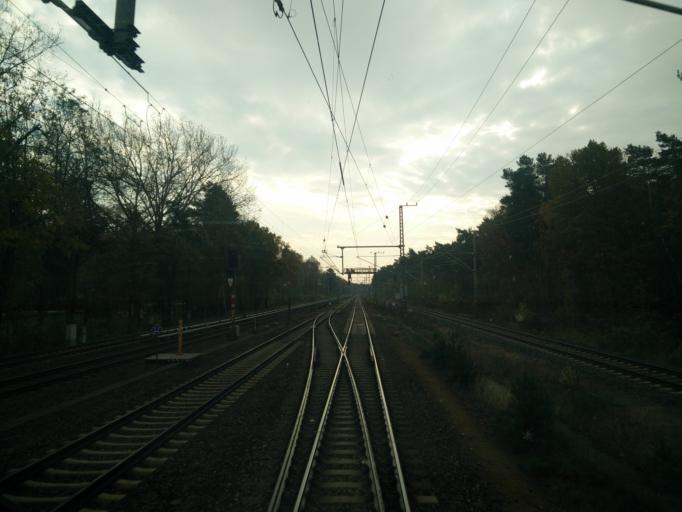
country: DE
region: Berlin
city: Grunau
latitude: 52.4035
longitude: 13.5873
